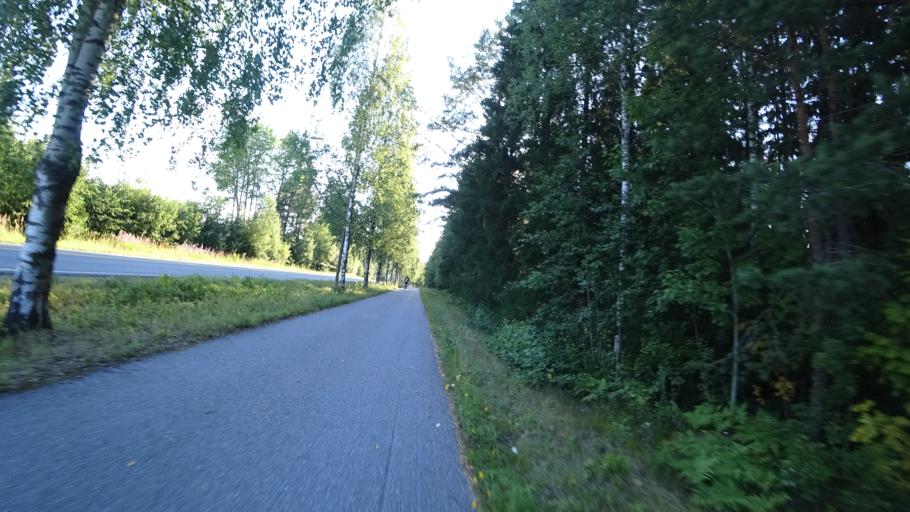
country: FI
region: Pirkanmaa
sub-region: Tampere
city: Nokia
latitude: 61.4664
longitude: 23.4316
